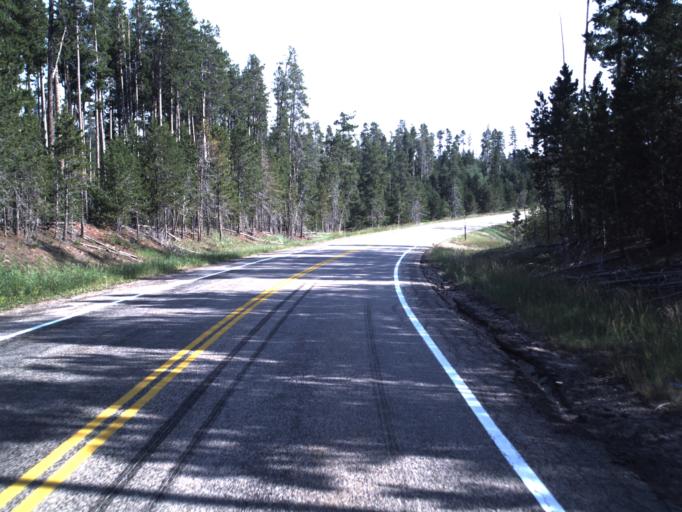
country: US
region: Utah
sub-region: Daggett County
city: Manila
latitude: 40.8446
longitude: -109.4655
